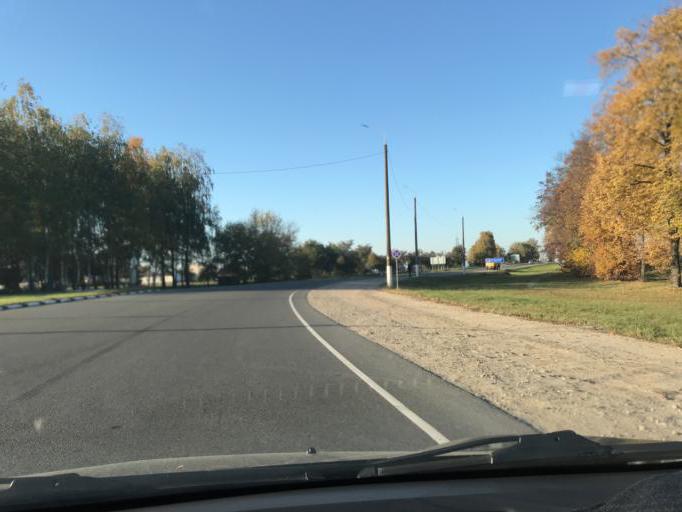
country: BY
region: Minsk
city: Slutsk
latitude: 53.0523
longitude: 27.5549
